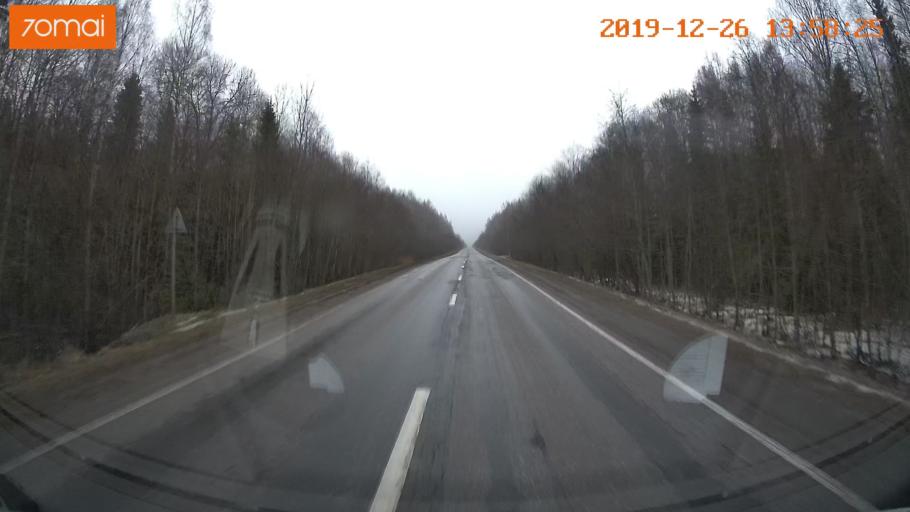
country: RU
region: Jaroslavl
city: Poshekhon'ye
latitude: 58.5742
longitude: 38.7004
